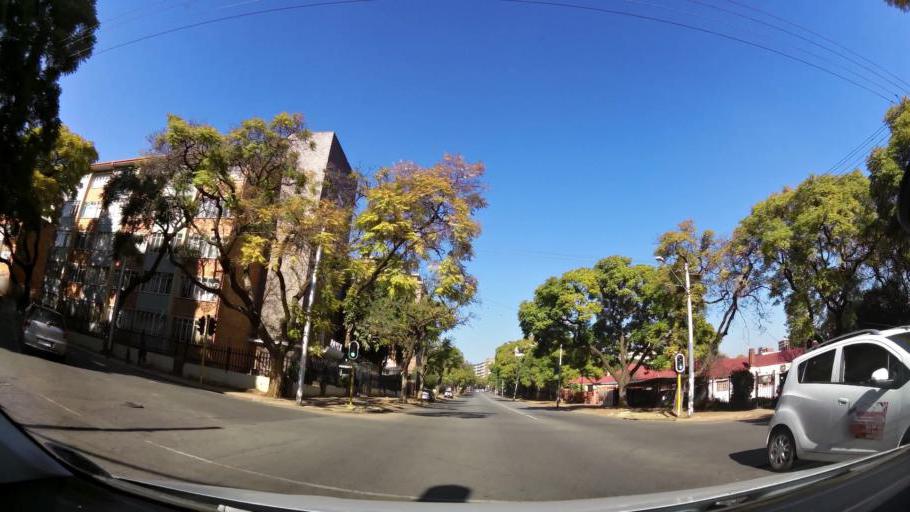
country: ZA
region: Gauteng
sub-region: City of Tshwane Metropolitan Municipality
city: Pretoria
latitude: -25.7558
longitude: 28.2068
